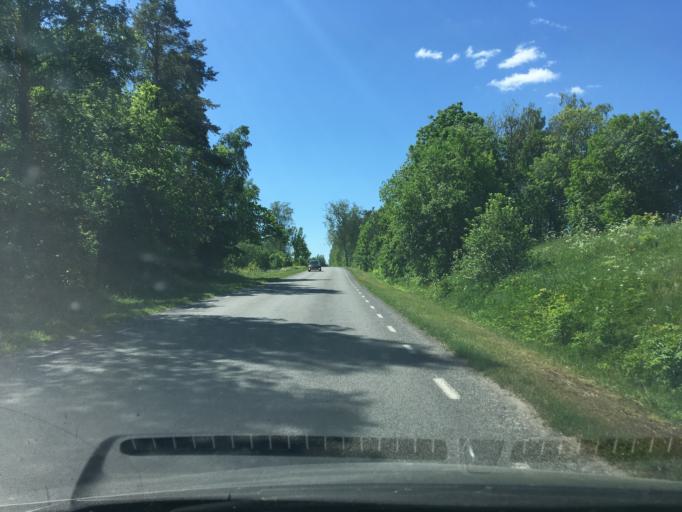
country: EE
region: Raplamaa
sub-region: Kohila vald
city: Kohila
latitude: 59.1012
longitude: 24.8141
